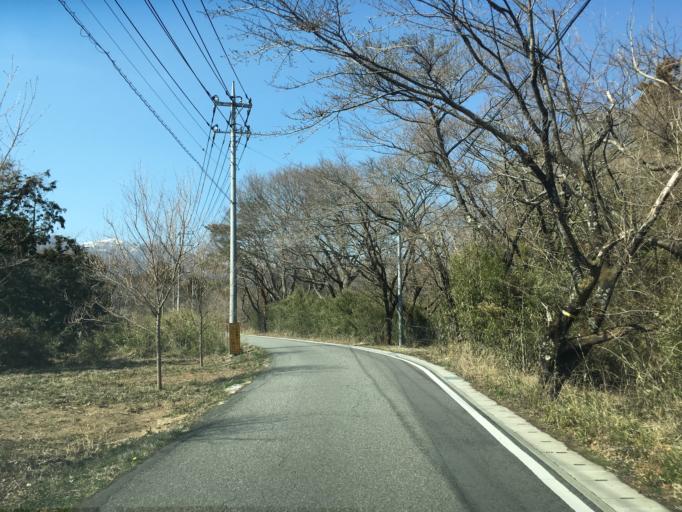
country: JP
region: Tochigi
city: Kuroiso
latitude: 37.0607
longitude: 140.0059
